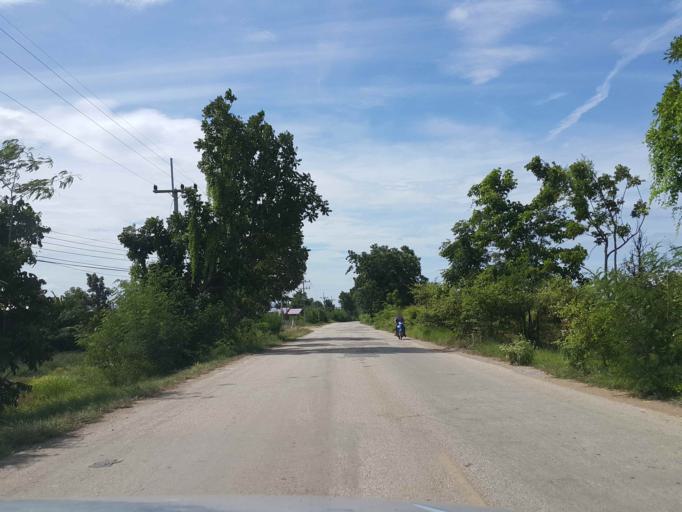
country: TH
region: Sukhothai
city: Ban Dan Lan Hoi
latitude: 17.1449
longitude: 99.5227
